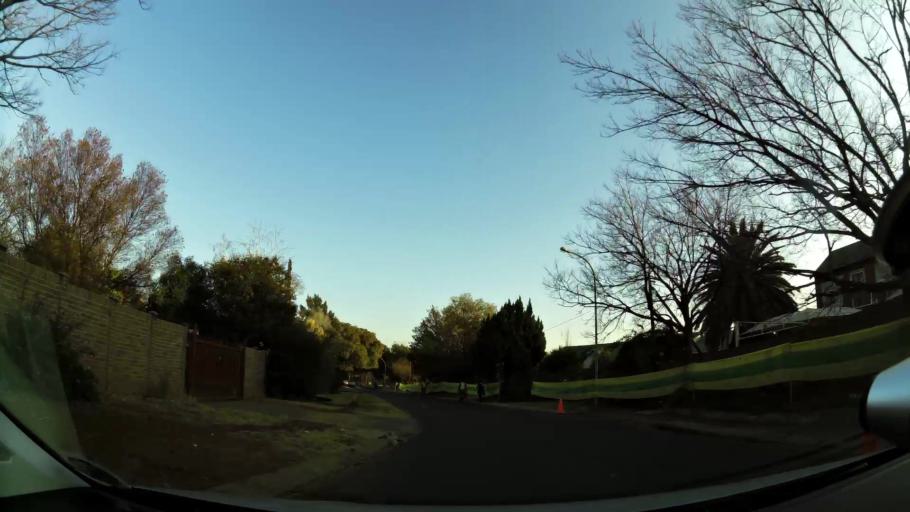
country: ZA
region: Orange Free State
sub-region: Mangaung Metropolitan Municipality
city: Bloemfontein
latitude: -29.0838
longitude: 26.1594
